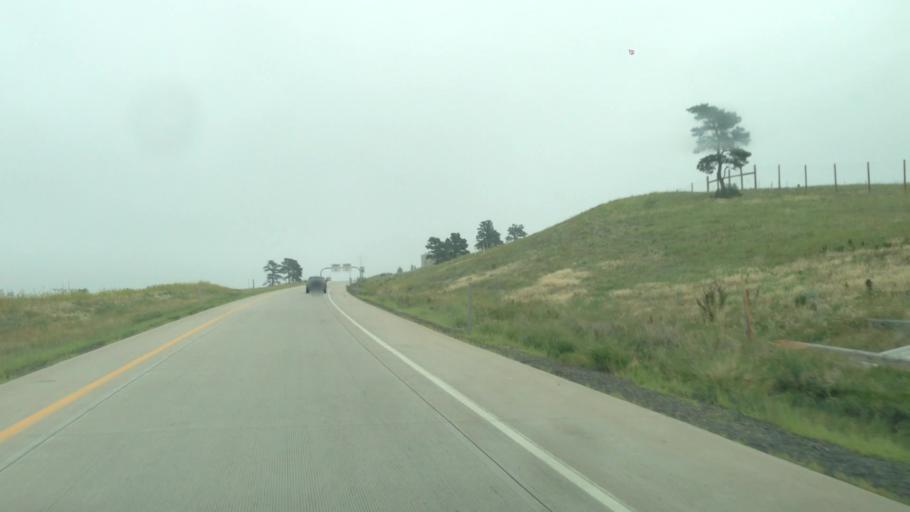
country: US
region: Colorado
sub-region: Douglas County
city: Parker
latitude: 39.5955
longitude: -104.7168
